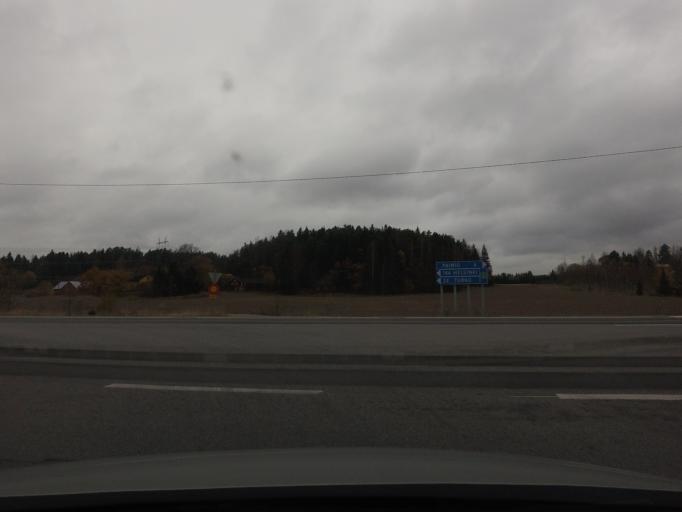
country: FI
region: Varsinais-Suomi
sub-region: Turku
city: Paimio
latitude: 60.4456
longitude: 22.6056
